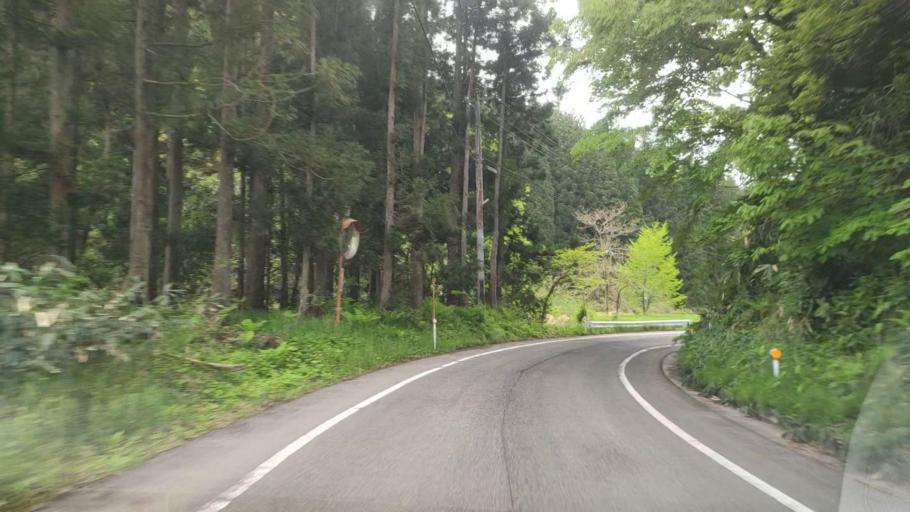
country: JP
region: Niigata
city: Gosen
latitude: 37.7138
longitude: 139.1227
